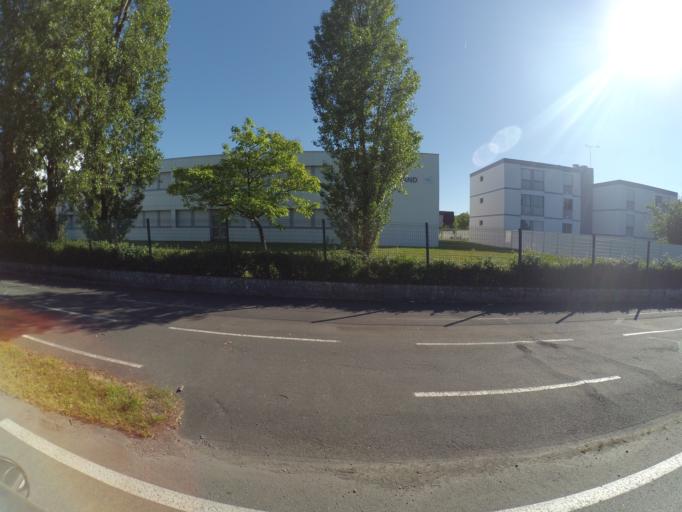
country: FR
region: Pays de la Loire
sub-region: Departement de la Vendee
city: Les Herbiers
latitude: 46.8617
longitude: -1.0214
